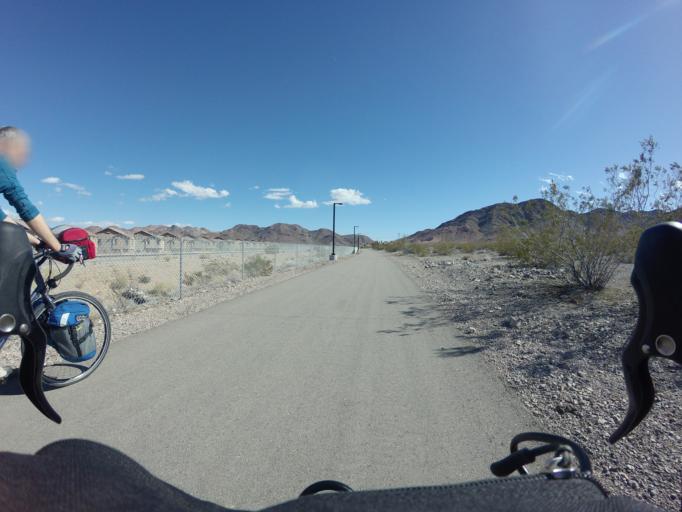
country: US
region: Nevada
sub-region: Clark County
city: Henderson
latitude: 35.9866
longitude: -114.9339
